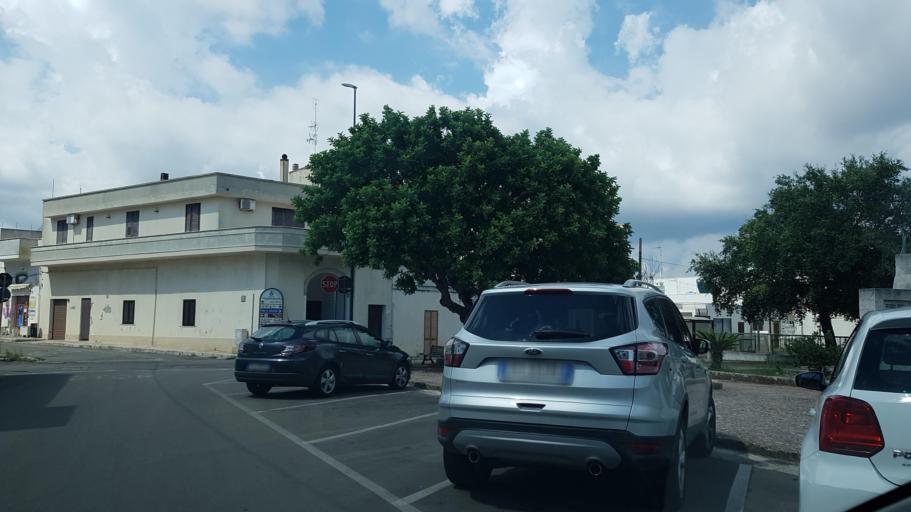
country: IT
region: Apulia
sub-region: Provincia di Lecce
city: Castrignano del Capo
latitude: 39.8316
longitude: 18.3523
